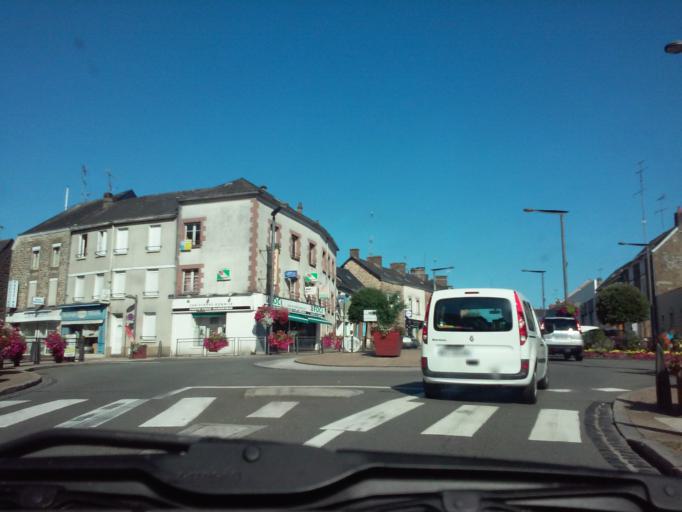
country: FR
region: Pays de la Loire
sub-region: Departement de la Mayenne
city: Ernee
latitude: 48.2968
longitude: -0.9351
